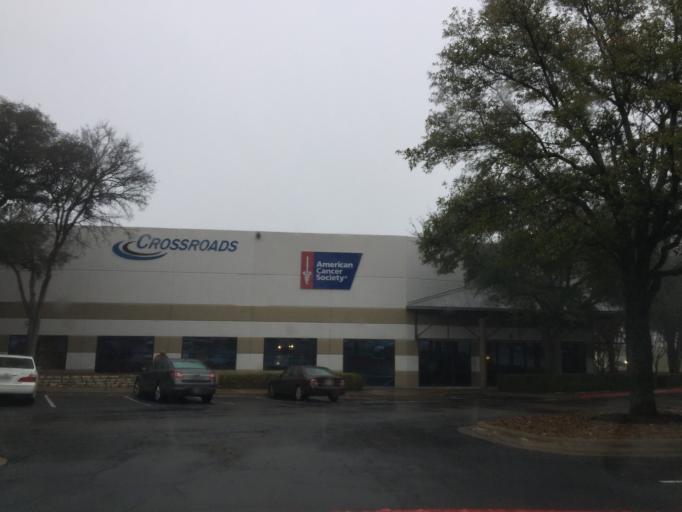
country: US
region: Texas
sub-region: Williamson County
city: Jollyville
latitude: 30.3994
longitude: -97.7323
